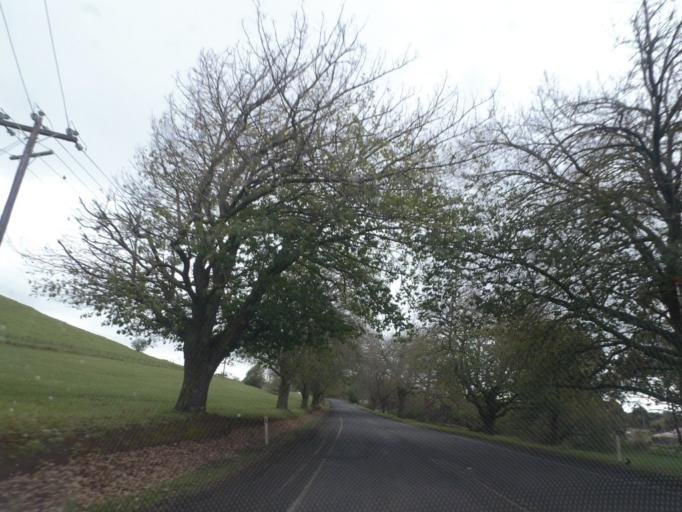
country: AU
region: Victoria
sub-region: Hume
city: Sunbury
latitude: -37.3441
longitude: 144.5328
